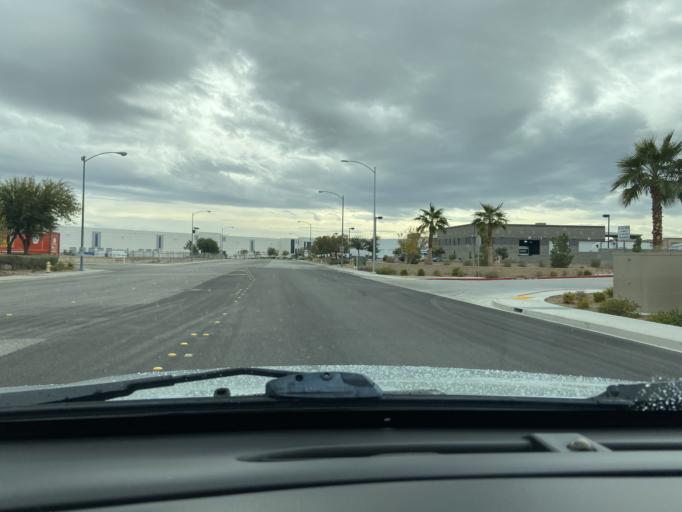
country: US
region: Nevada
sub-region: Clark County
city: North Las Vegas
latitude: 36.2439
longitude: -115.1079
